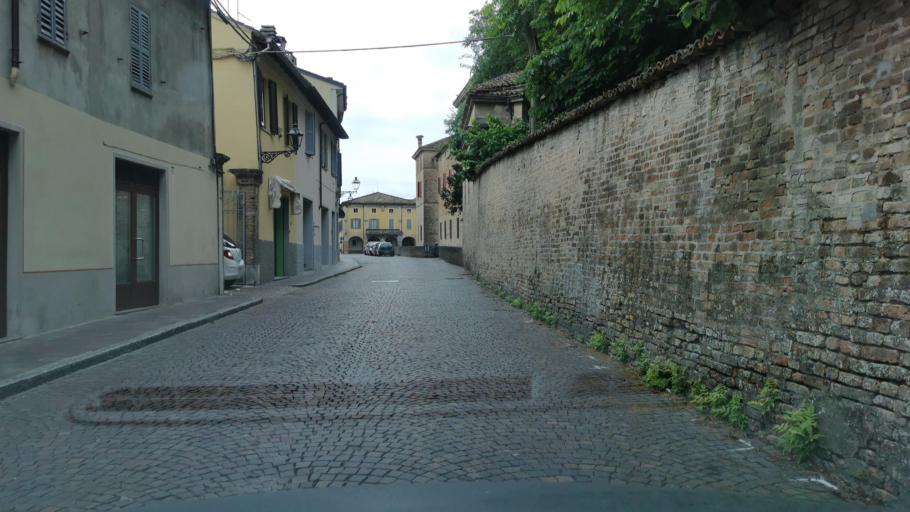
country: IT
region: Emilia-Romagna
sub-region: Provincia di Parma
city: Soragna
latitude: 44.9279
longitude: 10.1233
